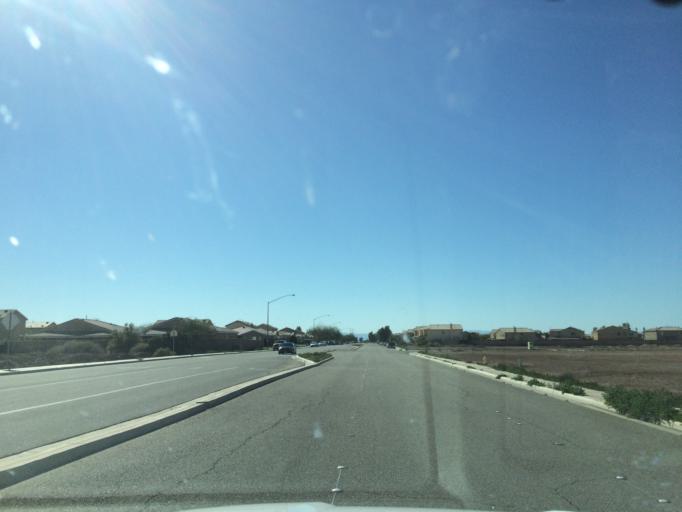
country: US
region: California
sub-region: Imperial County
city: Heber
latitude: 32.7380
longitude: -115.5351
